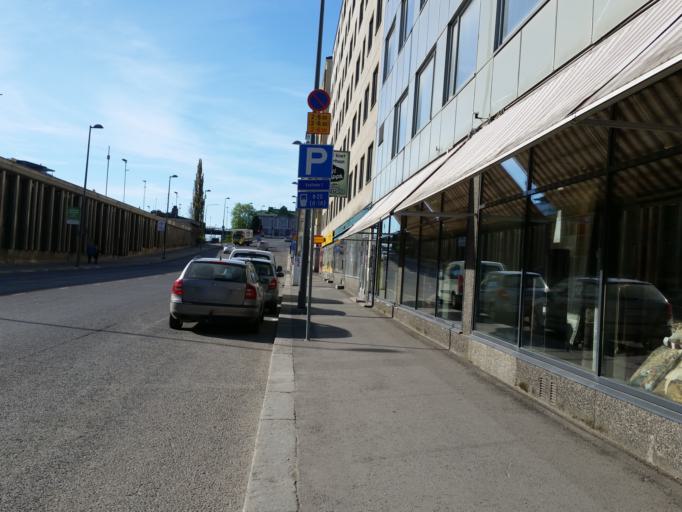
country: FI
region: Pirkanmaa
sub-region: Tampere
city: Tampere
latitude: 61.4973
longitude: 23.7721
